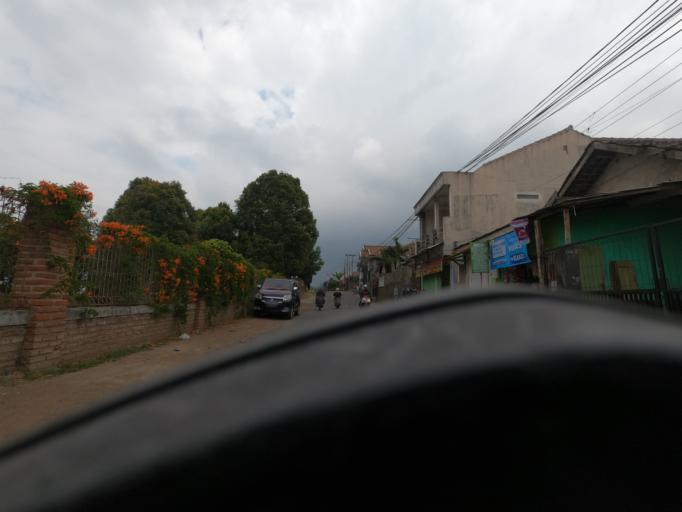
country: ID
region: West Java
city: Cimahi
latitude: -6.8161
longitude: 107.5520
